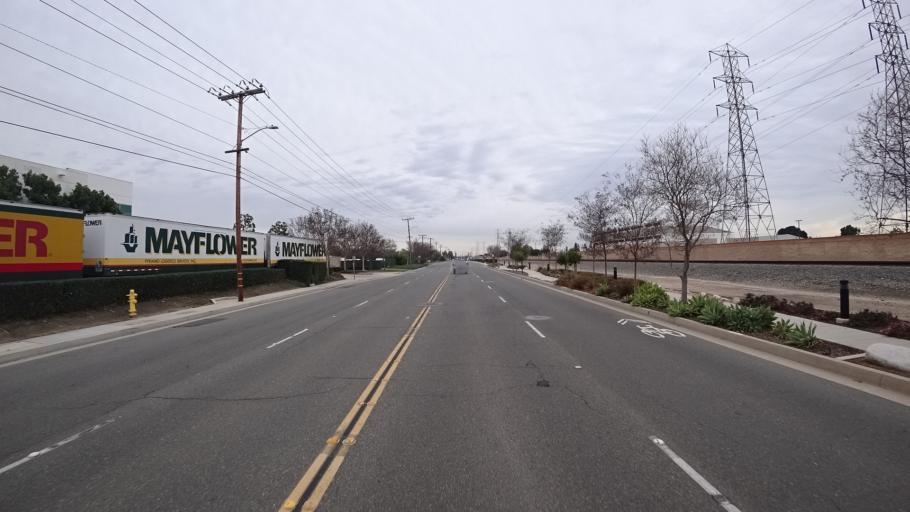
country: US
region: California
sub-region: Orange County
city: Midway City
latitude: 33.7492
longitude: -117.9984
